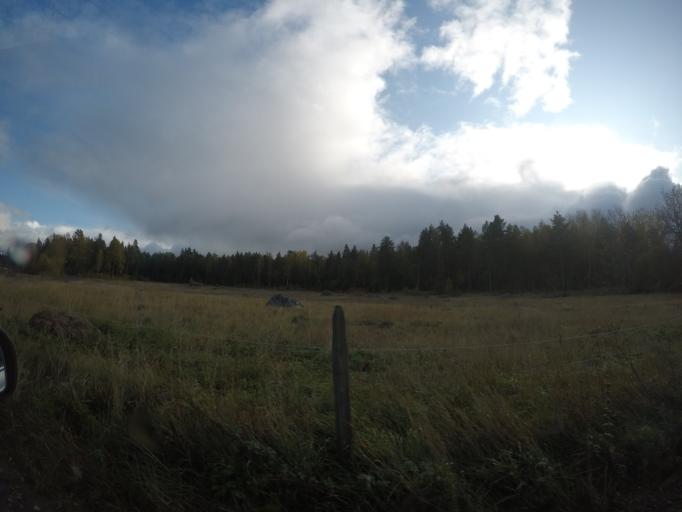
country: SE
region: Soedermanland
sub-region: Eskilstuna Kommun
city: Kvicksund
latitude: 59.3497
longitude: 16.3186
